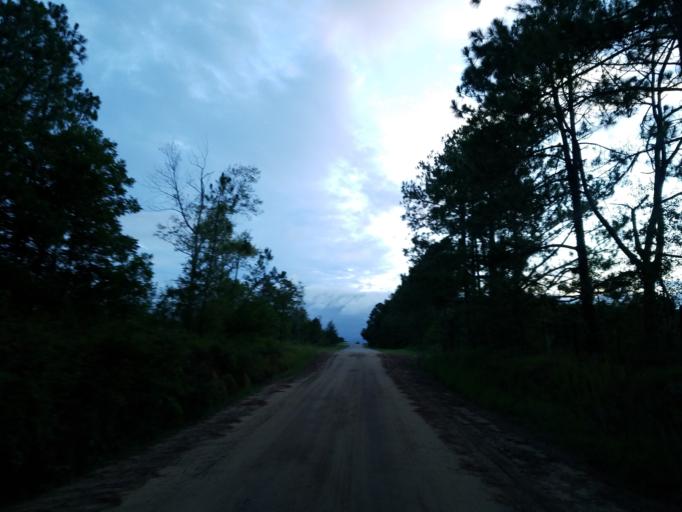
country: US
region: Georgia
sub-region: Tift County
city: Tifton
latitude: 31.5314
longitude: -83.5208
